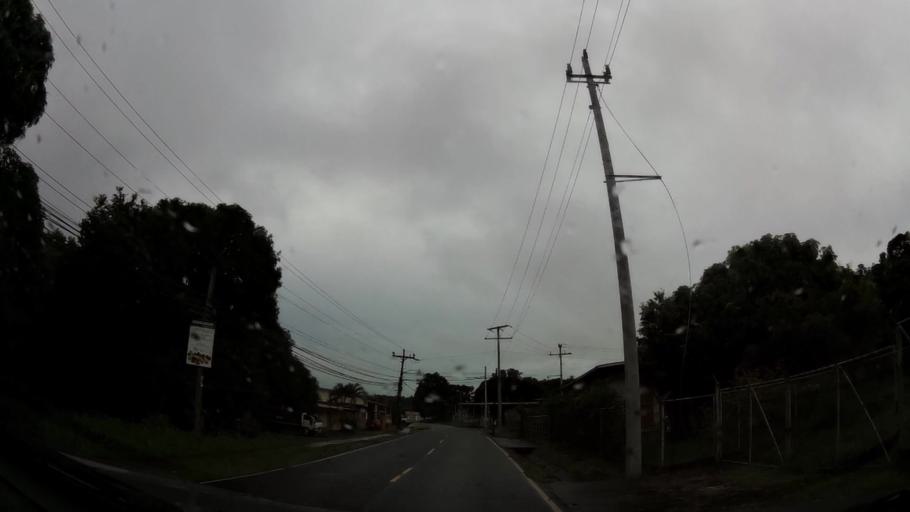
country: PA
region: Veraguas
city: Santiago de Veraguas
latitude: 8.0937
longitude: -80.9554
